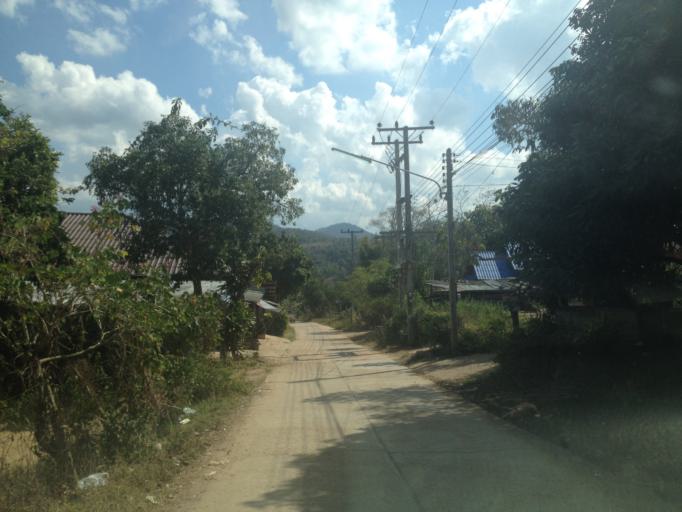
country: TH
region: Mae Hong Son
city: Ban Huai I Huak
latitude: 18.0890
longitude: 98.1955
